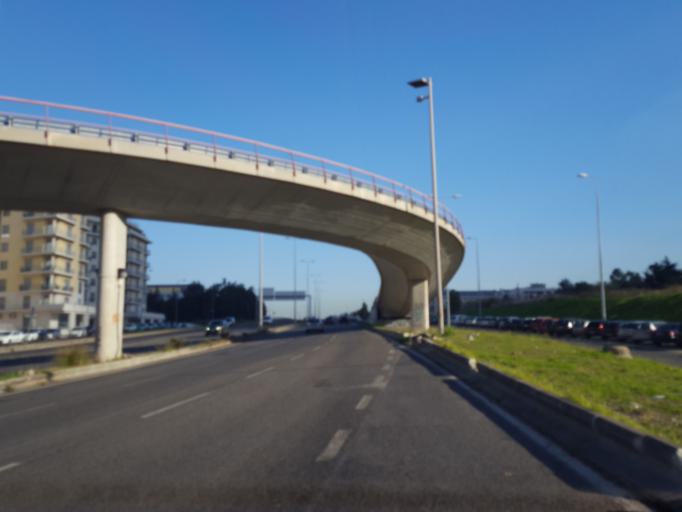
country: PT
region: Lisbon
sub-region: Odivelas
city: Pontinha
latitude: 38.7501
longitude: -9.1830
